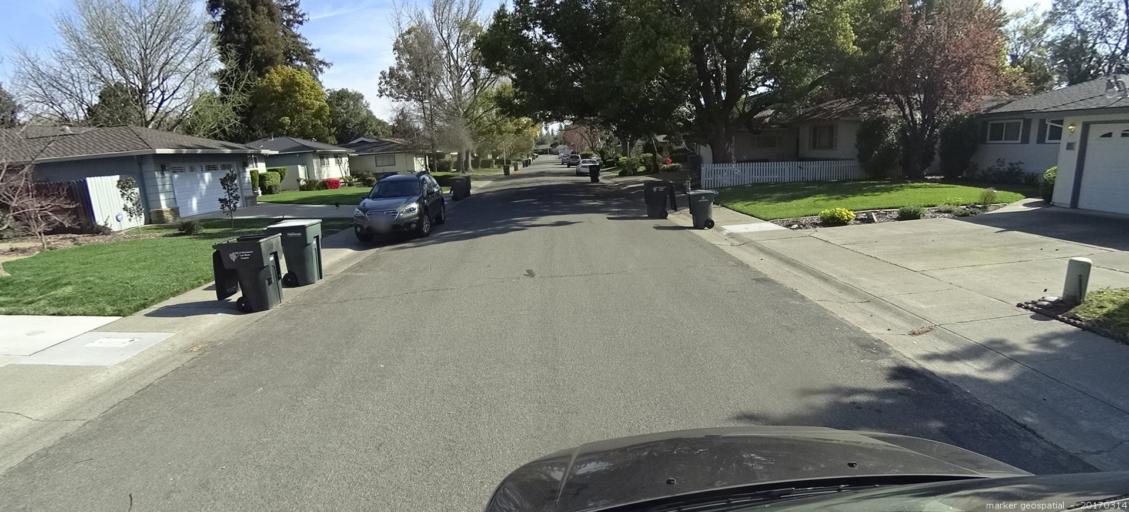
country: US
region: California
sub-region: Yolo County
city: West Sacramento
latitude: 38.5119
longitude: -121.5281
